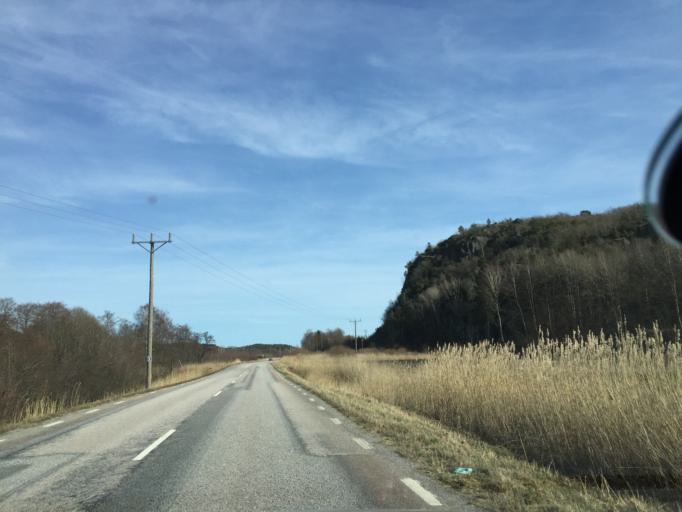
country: SE
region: Vaestra Goetaland
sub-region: Orust
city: Henan
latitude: 58.3438
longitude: 11.7525
